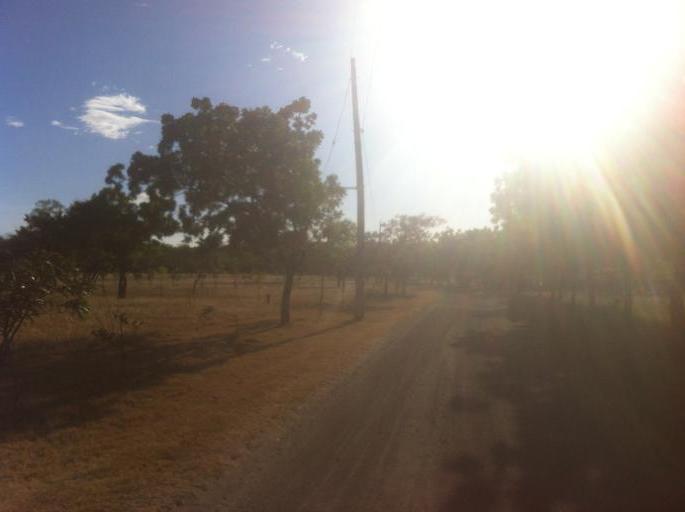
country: NI
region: Managua
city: Carlos Fonseca Amador
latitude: 11.9168
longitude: -86.5968
